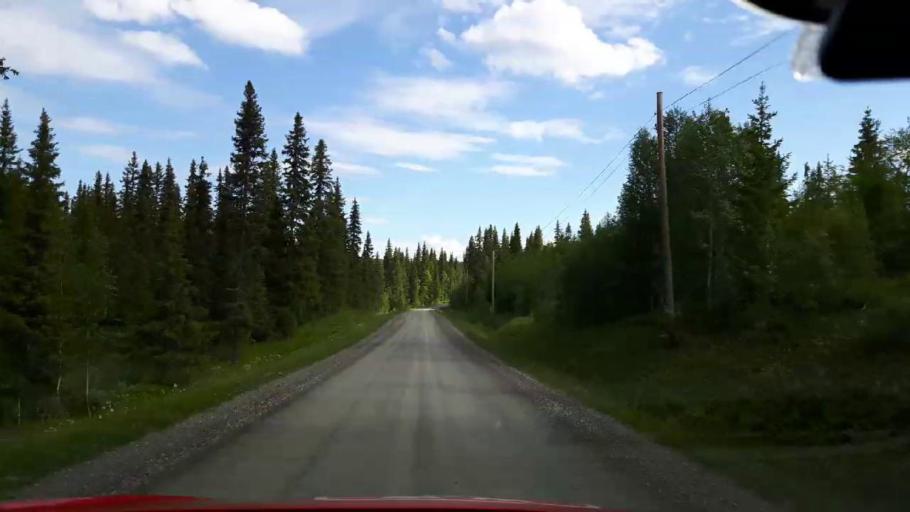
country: SE
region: Jaemtland
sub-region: Krokoms Kommun
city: Valla
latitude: 63.8154
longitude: 14.0473
